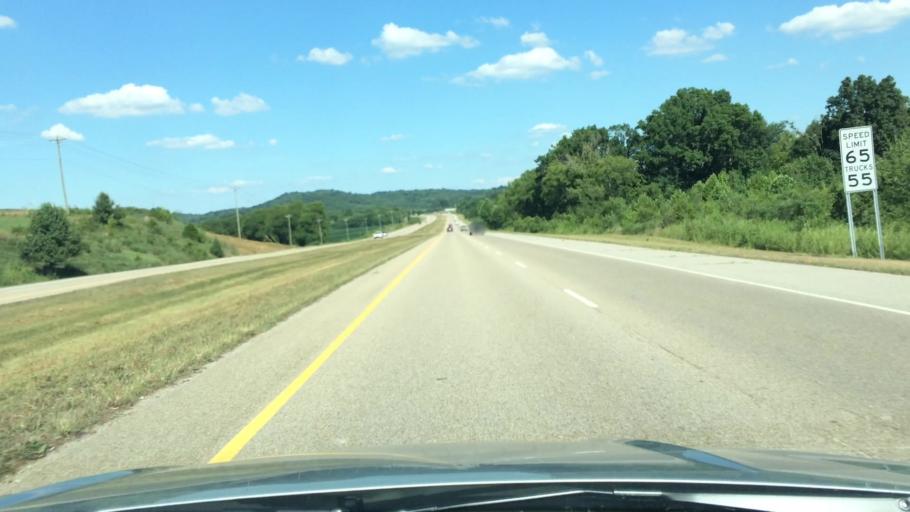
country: US
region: Tennessee
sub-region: Loudon County
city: Greenback
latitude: 35.7371
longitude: -84.1852
